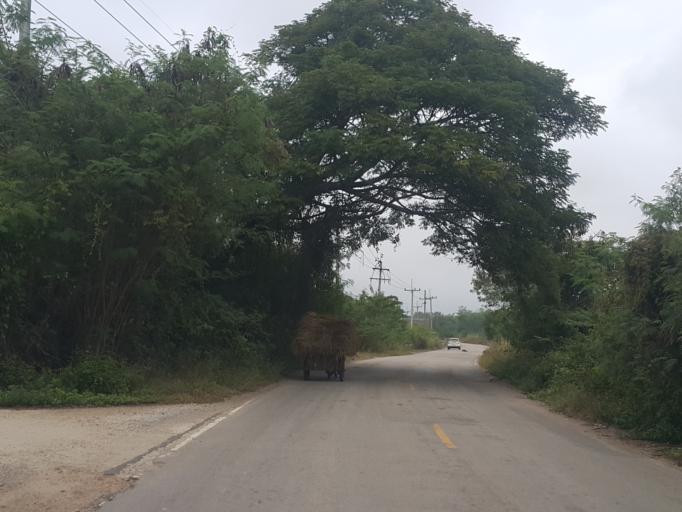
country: TH
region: Lampang
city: Lampang
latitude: 18.3273
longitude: 99.4871
